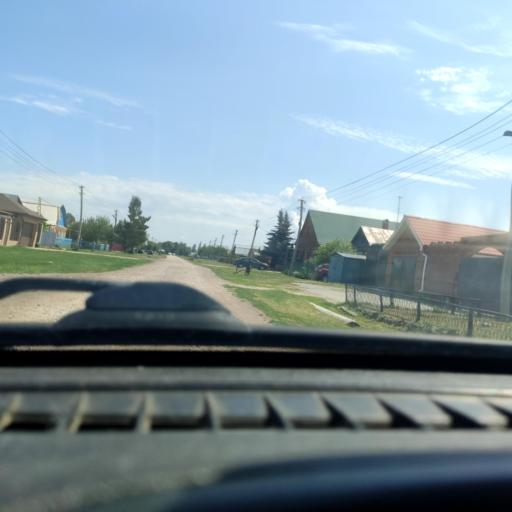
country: RU
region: Samara
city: Tol'yatti
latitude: 53.6363
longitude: 49.2919
